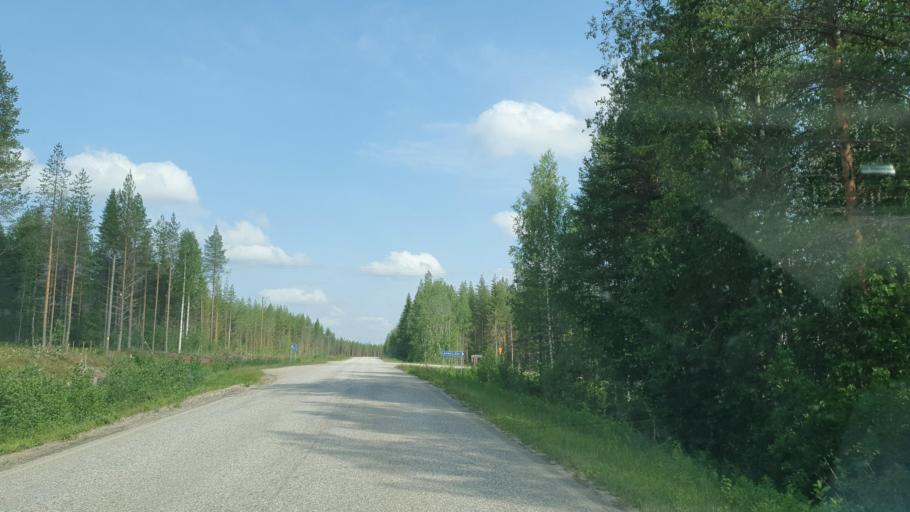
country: FI
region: Kainuu
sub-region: Kehys-Kainuu
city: Kuhmo
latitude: 64.0376
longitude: 29.9420
